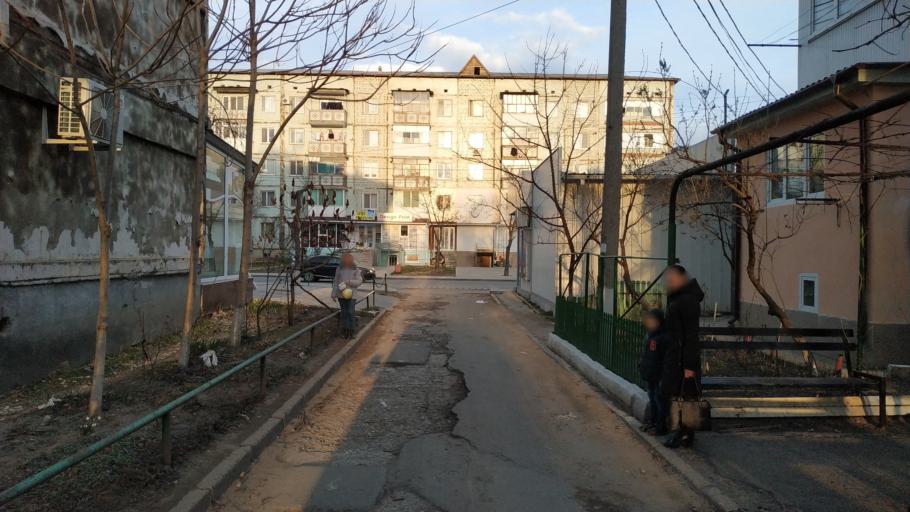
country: MD
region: Hincesti
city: Hincesti
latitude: 46.8299
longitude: 28.5914
